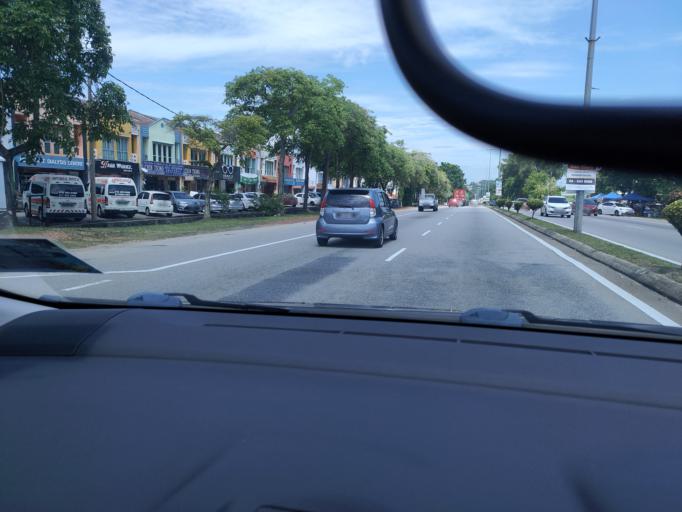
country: MY
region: Melaka
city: Bukit Rambai
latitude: 2.2764
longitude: 102.2154
